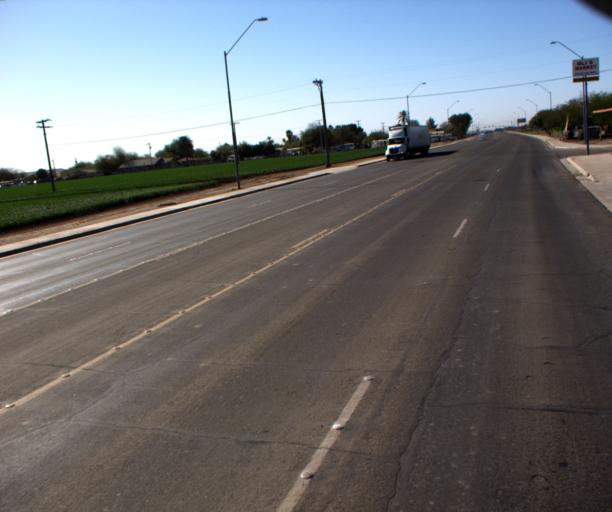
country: US
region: Arizona
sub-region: Yuma County
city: San Luis
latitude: 32.5580
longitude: -114.7848
